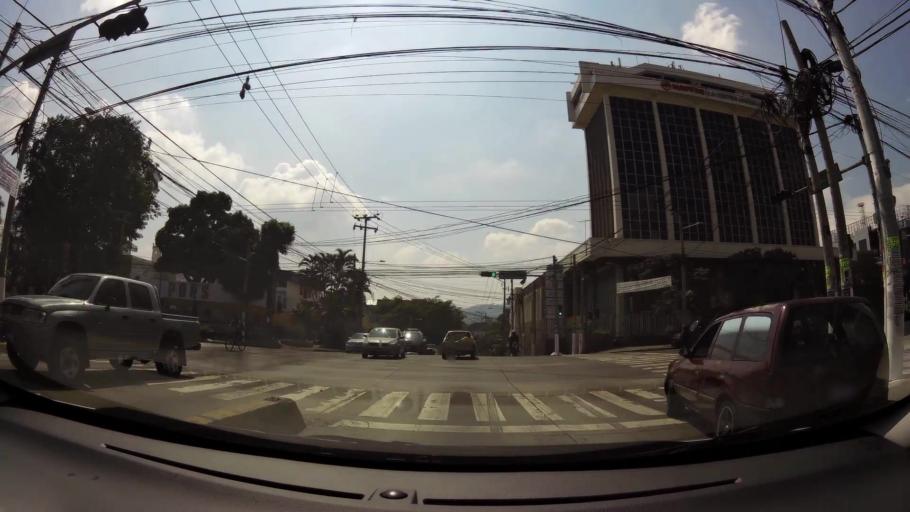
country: SV
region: San Salvador
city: San Salvador
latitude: 13.7011
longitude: -89.2208
